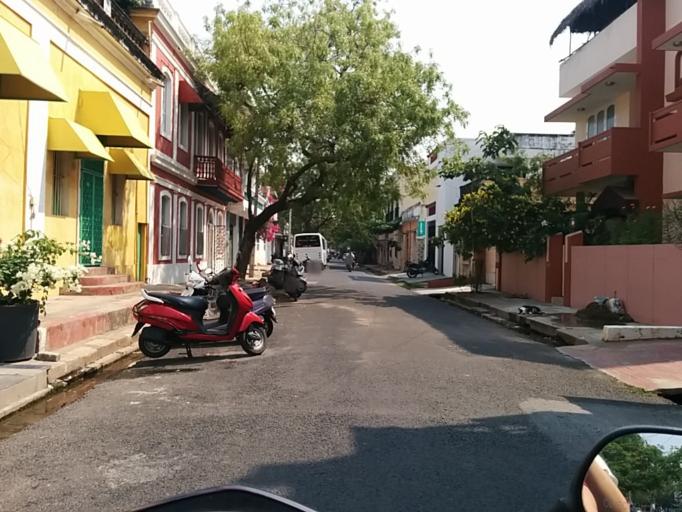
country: IN
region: Pondicherry
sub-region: Puducherry
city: Puducherry
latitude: 11.9275
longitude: 79.8322
